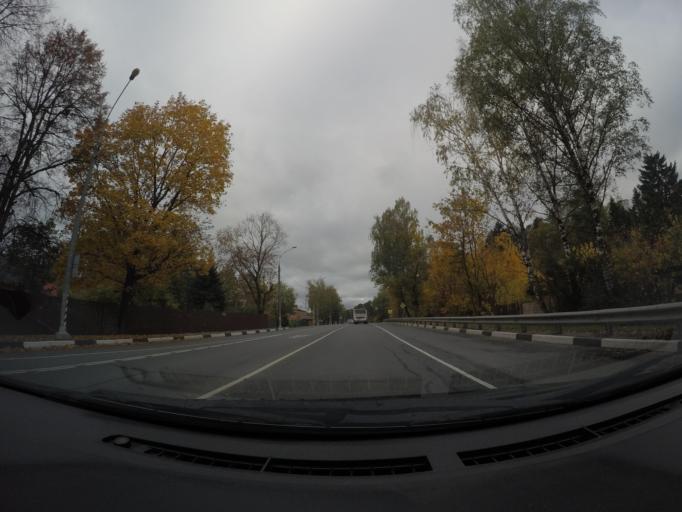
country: RU
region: Moskovskaya
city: Dorokhovo
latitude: 55.6416
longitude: 36.3269
